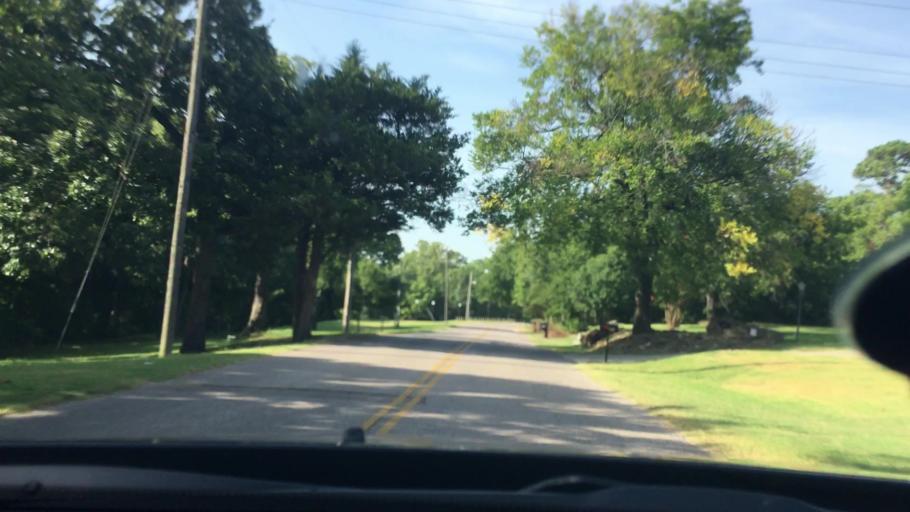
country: US
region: Oklahoma
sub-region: Pontotoc County
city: Ada
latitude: 34.7600
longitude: -96.6553
